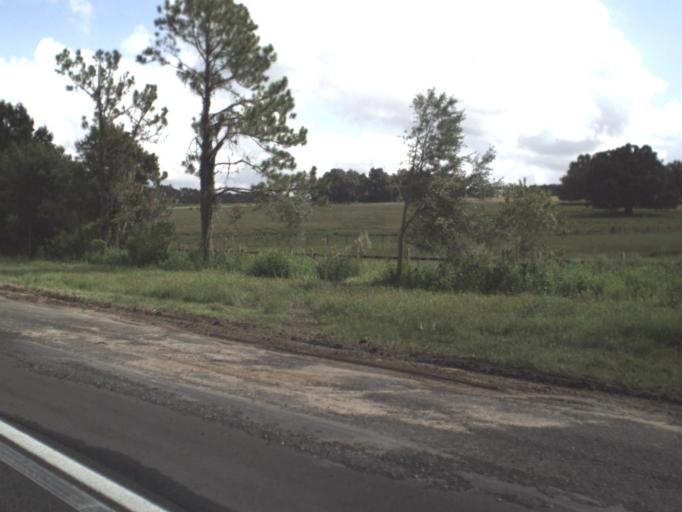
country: US
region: Florida
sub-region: Pasco County
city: San Antonio
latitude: 28.3925
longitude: -82.3192
